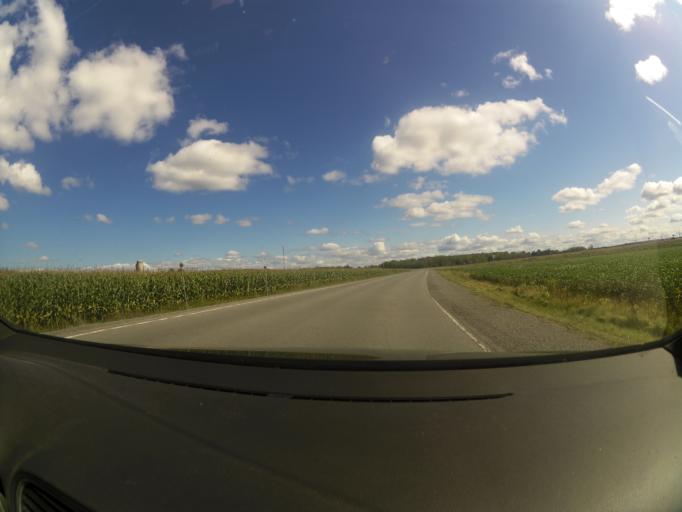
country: CA
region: Ontario
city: Carleton Place
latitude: 45.1536
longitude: -76.0934
